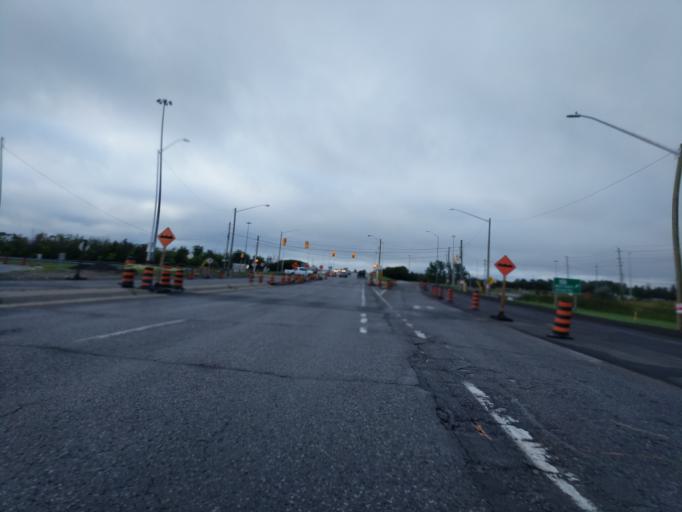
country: CA
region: Ontario
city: Bells Corners
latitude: 45.3413
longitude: -75.8421
